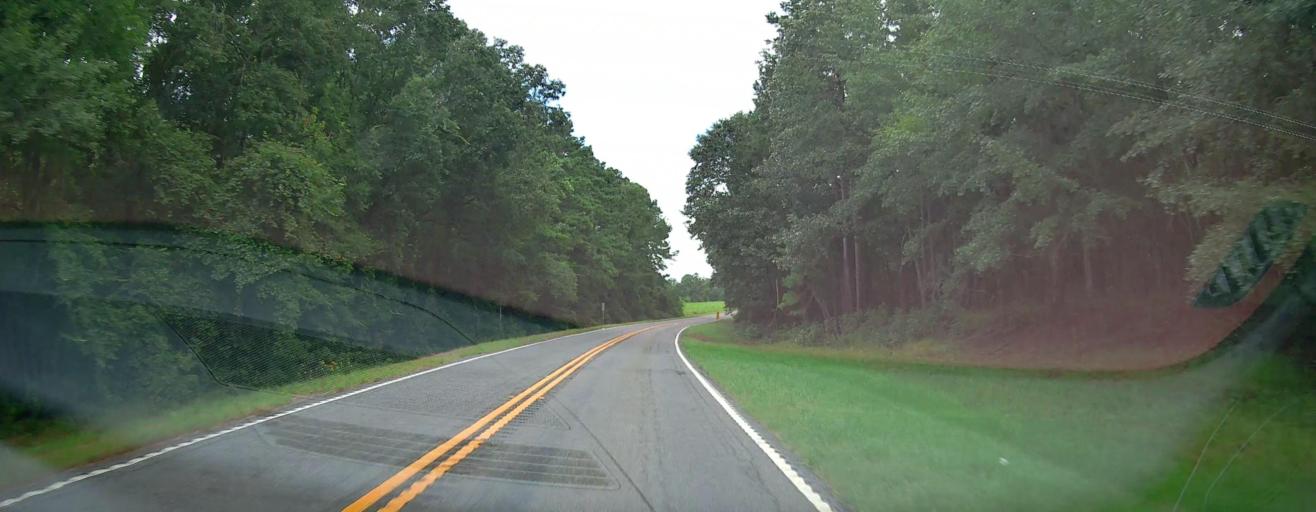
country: US
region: Georgia
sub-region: Dooly County
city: Unadilla
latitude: 32.2831
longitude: -83.8238
